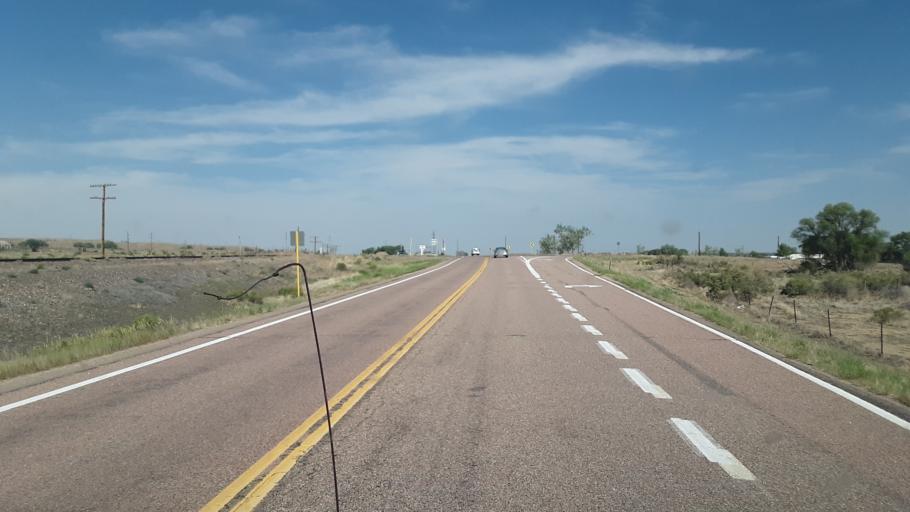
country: US
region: Colorado
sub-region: Otero County
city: Fowler
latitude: 38.1555
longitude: -104.0248
